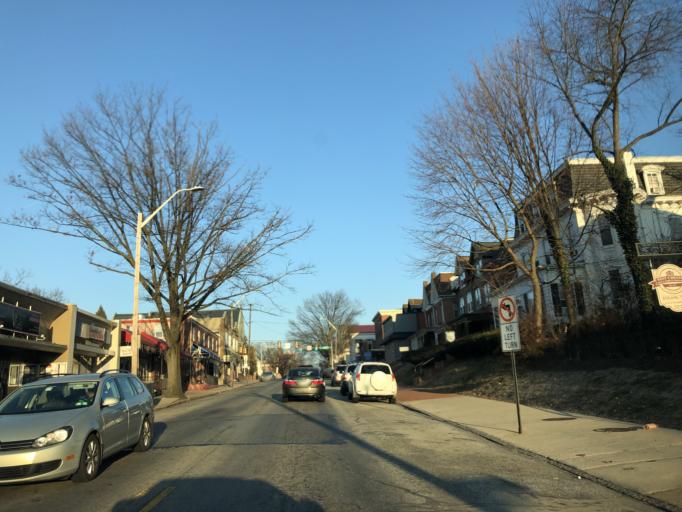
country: US
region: Pennsylvania
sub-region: Chester County
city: West Chester
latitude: 39.9565
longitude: -75.6010
